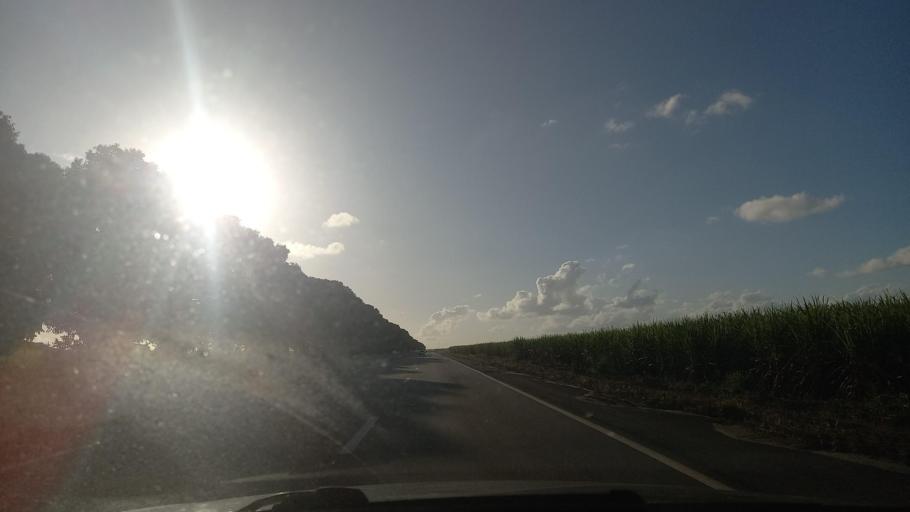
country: BR
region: Alagoas
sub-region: Campo Alegre
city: Campo Alegre
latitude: -9.8142
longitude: -36.2529
